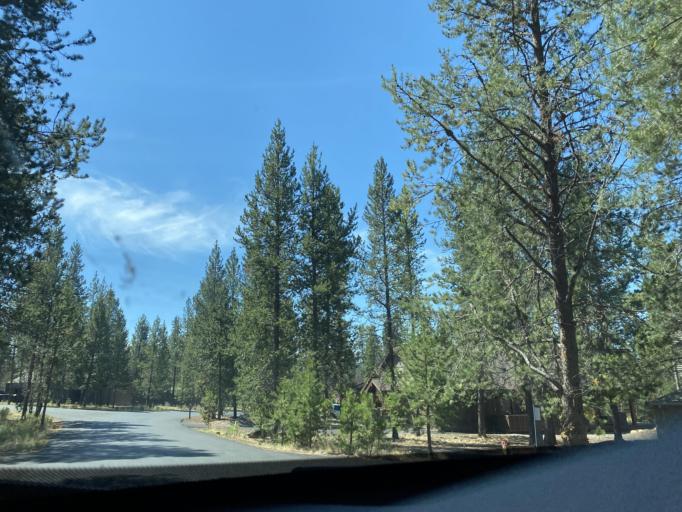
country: US
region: Oregon
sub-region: Deschutes County
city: Sunriver
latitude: 43.8954
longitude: -121.4380
